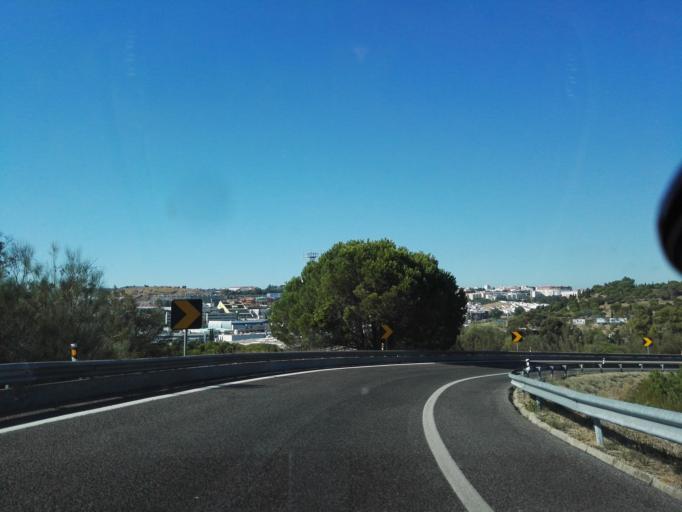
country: PT
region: Lisbon
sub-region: Oeiras
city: Alges
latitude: 38.7198
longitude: -9.2111
